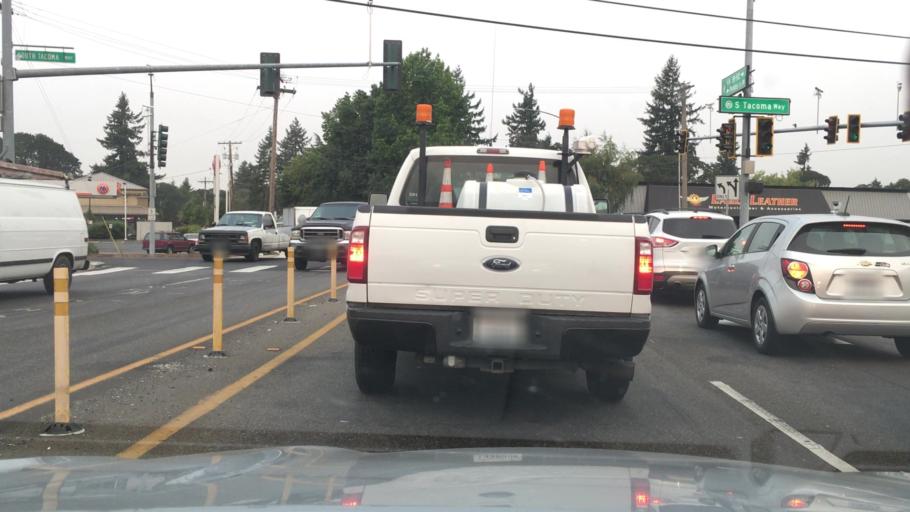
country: US
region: Washington
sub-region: Pierce County
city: McChord Air Force Base
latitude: 47.1640
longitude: -122.4832
